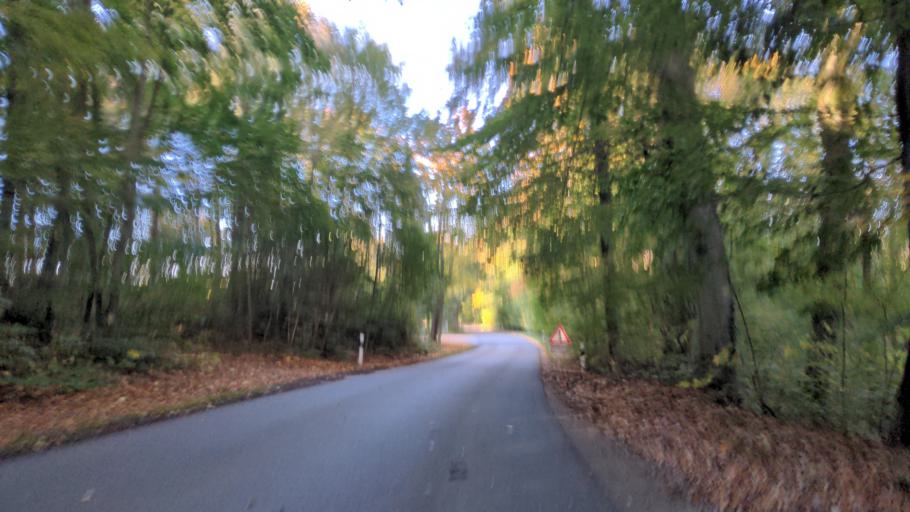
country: DE
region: Schleswig-Holstein
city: Kirchnuchel
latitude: 54.1554
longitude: 10.6687
